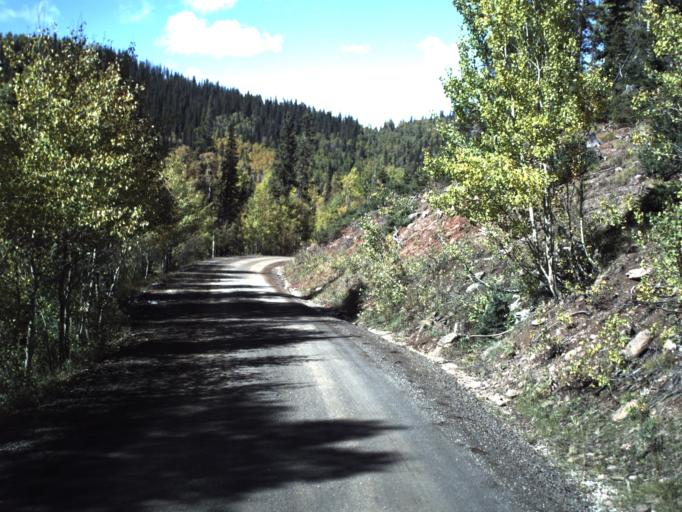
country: US
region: Utah
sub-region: Piute County
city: Junction
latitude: 38.3101
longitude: -112.3640
